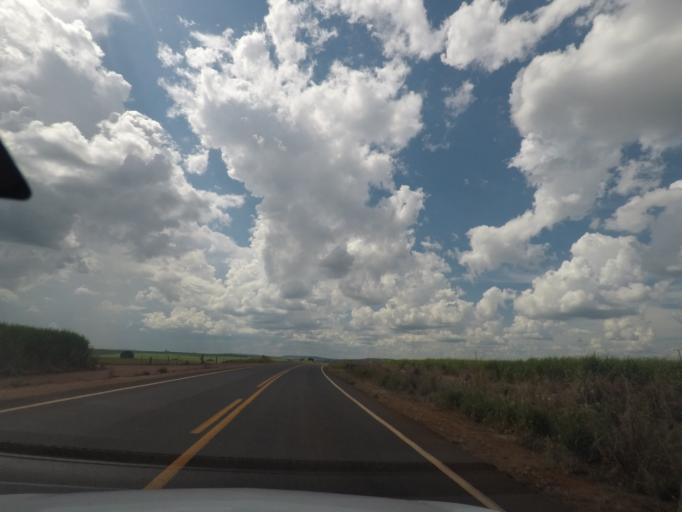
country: BR
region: Minas Gerais
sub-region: Conceicao Das Alagoas
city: Conceicao das Alagoas
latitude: -19.8290
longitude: -48.5915
